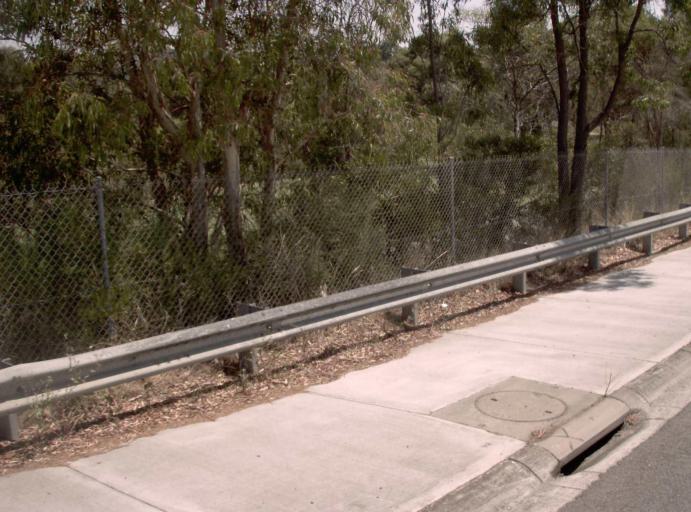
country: AU
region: Victoria
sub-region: Manningham
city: Bulleen
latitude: -37.7780
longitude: 145.0785
